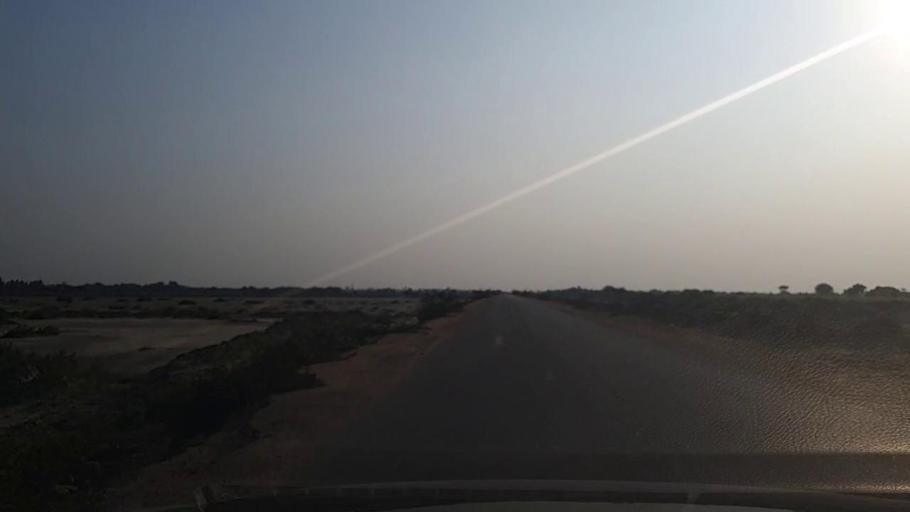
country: PK
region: Sindh
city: Mirpur Sakro
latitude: 24.5194
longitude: 67.8227
